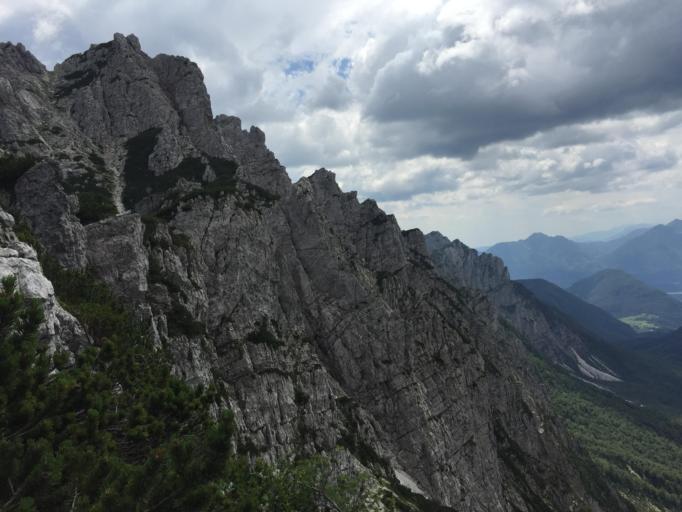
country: IT
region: Friuli Venezia Giulia
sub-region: Provincia di Udine
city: Paularo
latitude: 46.4684
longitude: 13.1330
